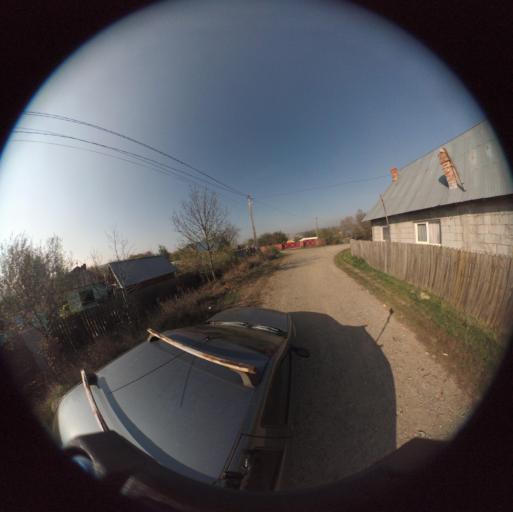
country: RO
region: Vaslui
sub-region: Comuna Bacesti
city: Bacesti
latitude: 46.8282
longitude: 27.2552
